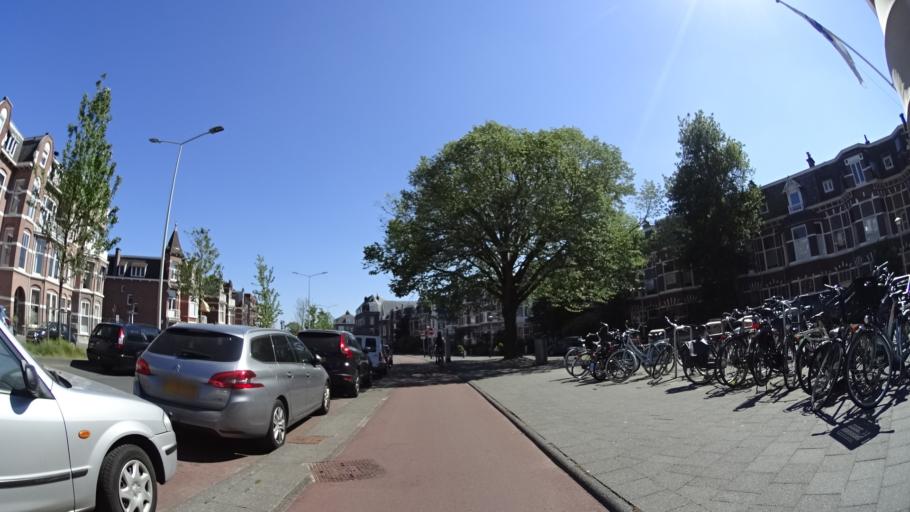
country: NL
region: South Holland
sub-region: Gemeente Den Haag
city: The Hague
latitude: 52.0801
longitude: 4.2762
